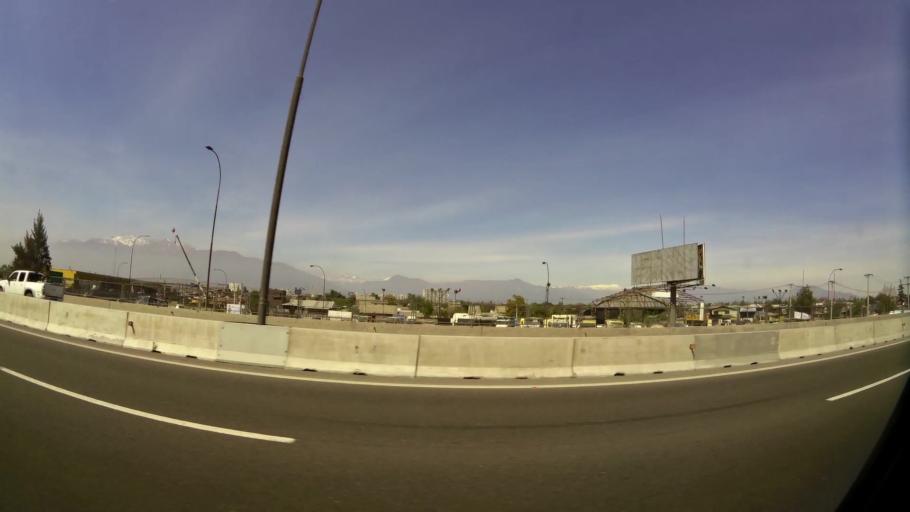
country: CL
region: Santiago Metropolitan
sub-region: Provincia de Maipo
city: San Bernardo
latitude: -33.5331
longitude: -70.6823
